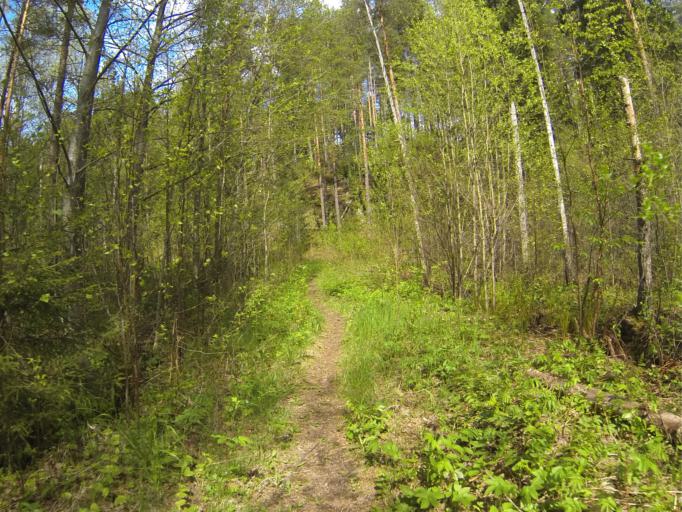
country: FI
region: Varsinais-Suomi
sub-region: Salo
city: Halikko
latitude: 60.3289
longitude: 23.0697
